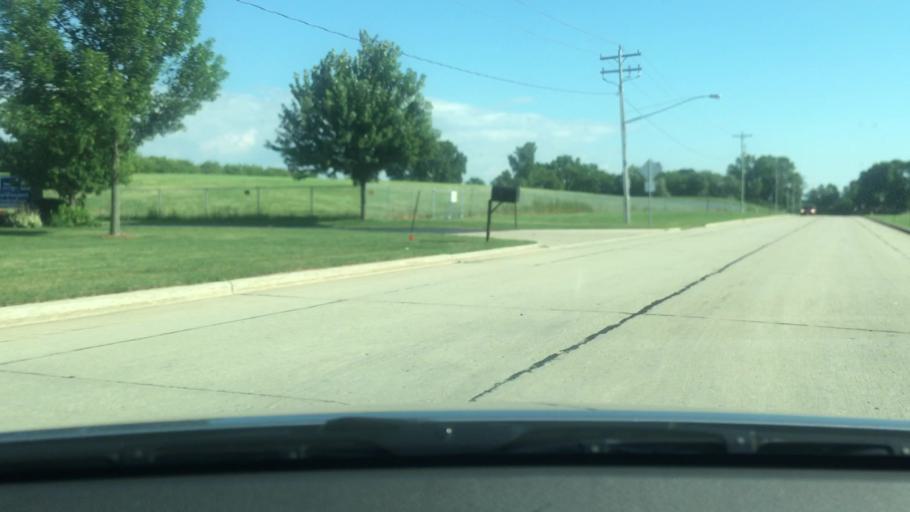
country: US
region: Wisconsin
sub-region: Winnebago County
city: Oshkosh
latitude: 43.9758
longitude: -88.5498
